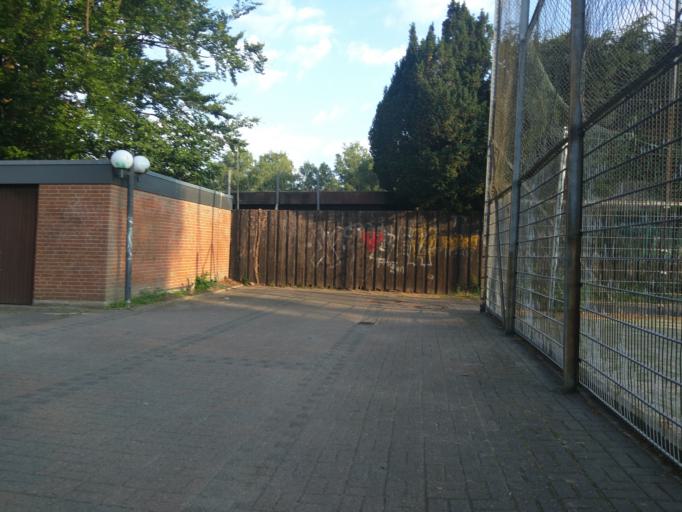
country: DE
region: Schleswig-Holstein
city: Grosshansdorf
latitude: 53.6487
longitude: 10.2770
